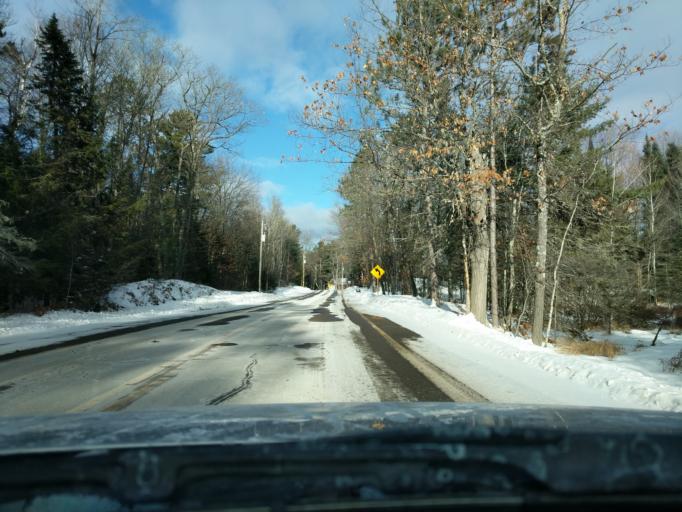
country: US
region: Wisconsin
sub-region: Vilas County
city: Eagle River
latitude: 45.7788
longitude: -89.0748
